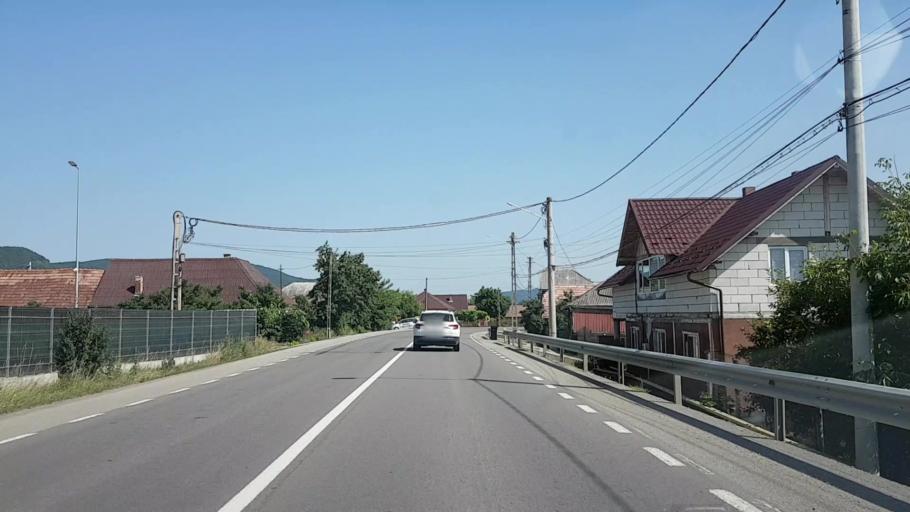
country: RO
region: Bistrita-Nasaud
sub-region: Comuna Sieu-Magherus
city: Sieu-Magherus
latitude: 47.0967
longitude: 24.3670
